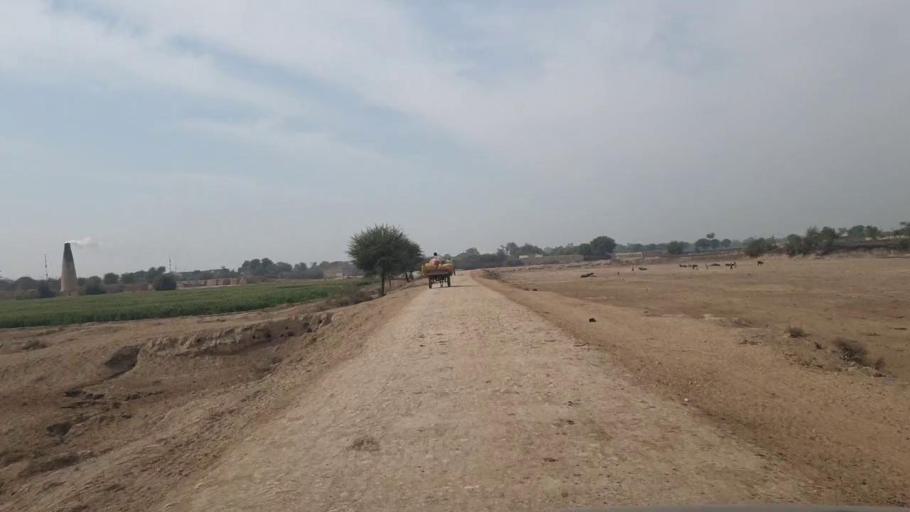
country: PK
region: Sindh
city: Shahdadpur
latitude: 25.9400
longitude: 68.6370
